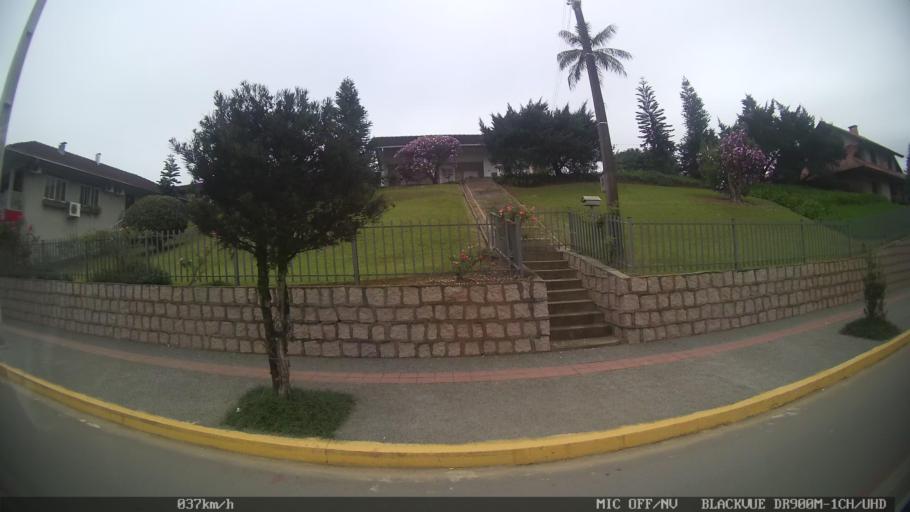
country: BR
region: Santa Catarina
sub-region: Joinville
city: Joinville
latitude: -26.2092
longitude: -48.9072
